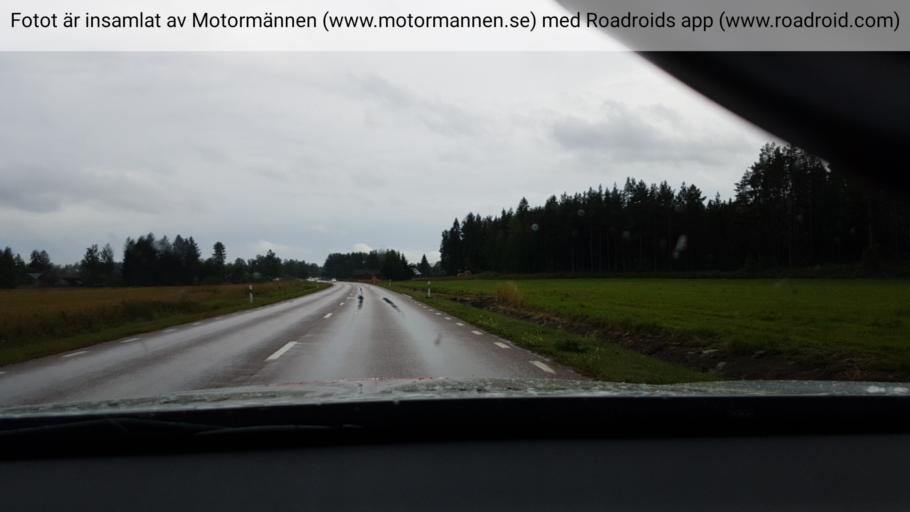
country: SE
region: Uppsala
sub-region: Tierps Kommun
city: Karlholmsbruk
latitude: 60.4478
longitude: 17.7727
